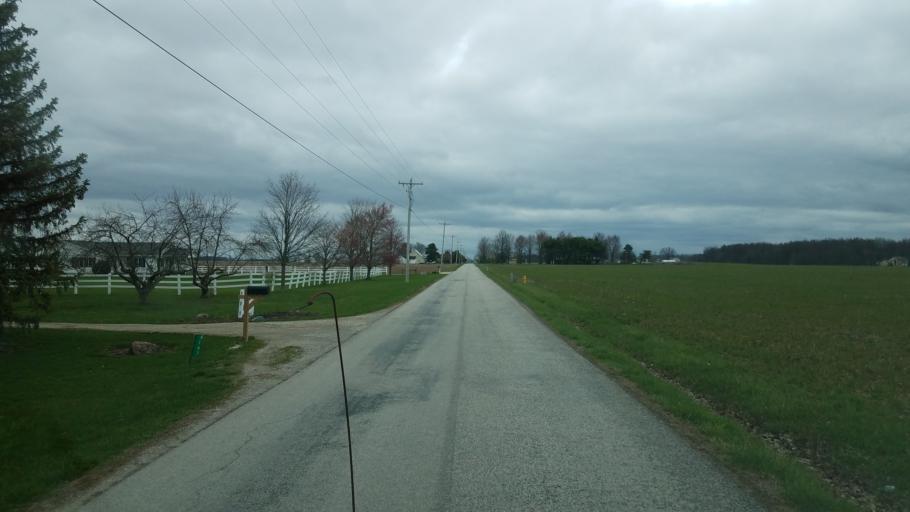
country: US
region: Ohio
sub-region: Delaware County
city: Delaware
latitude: 40.3750
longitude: -83.1197
